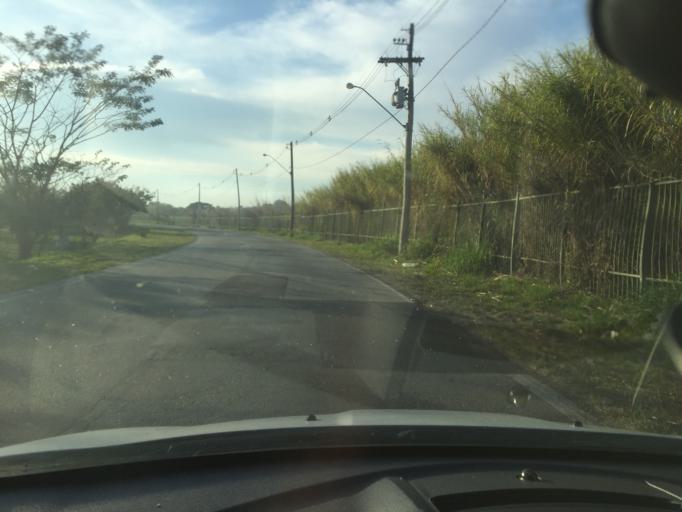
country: BR
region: Sao Paulo
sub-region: Jundiai
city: Jundiai
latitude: -23.2025
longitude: -46.8616
